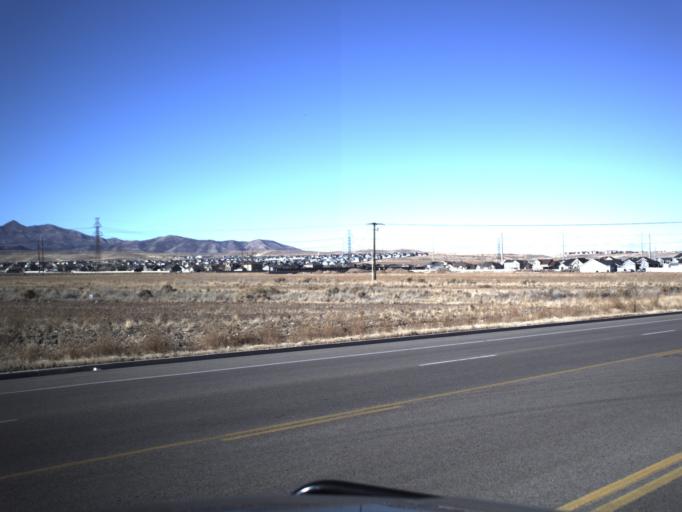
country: US
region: Utah
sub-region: Salt Lake County
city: Oquirrh
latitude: 40.5925
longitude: -112.0242
